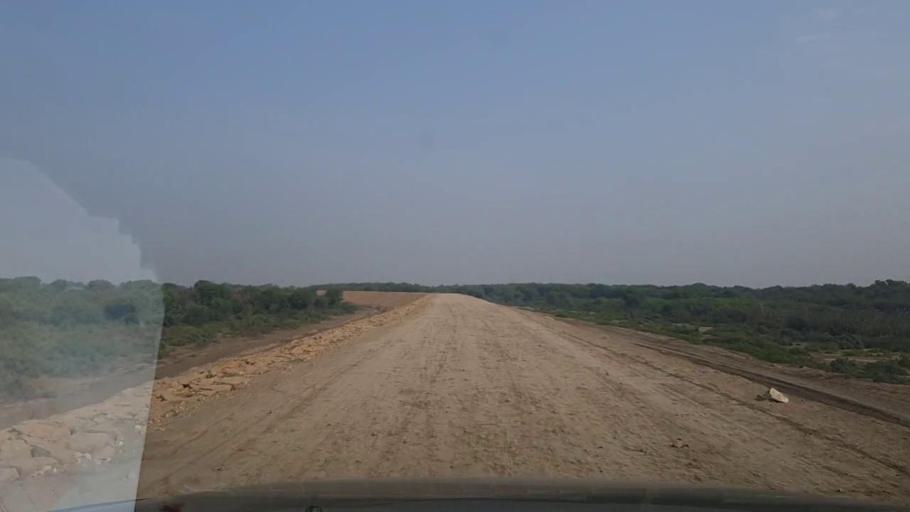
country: PK
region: Sindh
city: Bulri
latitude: 24.9696
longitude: 68.2906
